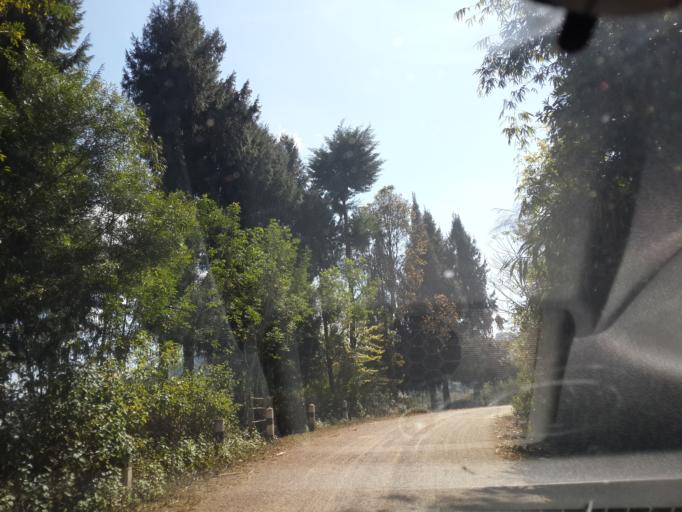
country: TH
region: Chiang Mai
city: Fang
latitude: 19.9405
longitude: 99.0423
